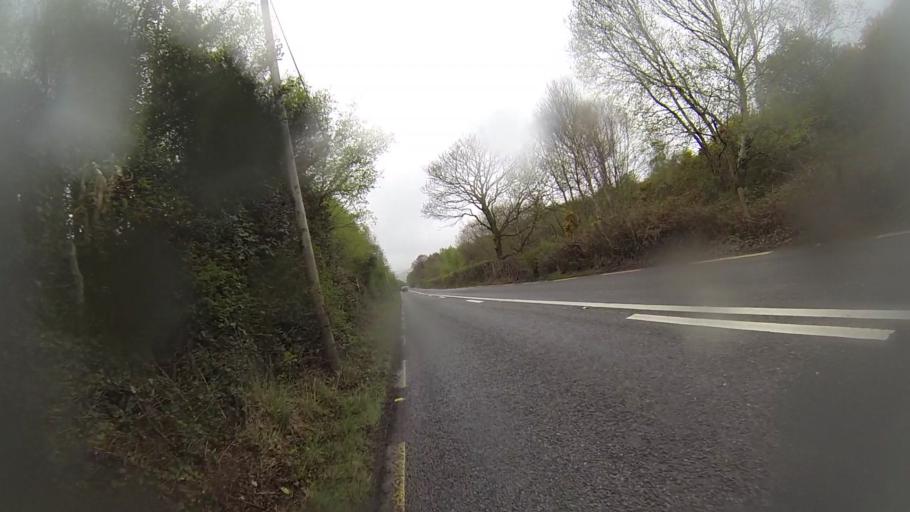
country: IE
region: Munster
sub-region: Ciarrai
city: Kenmare
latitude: 51.8130
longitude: -9.5498
